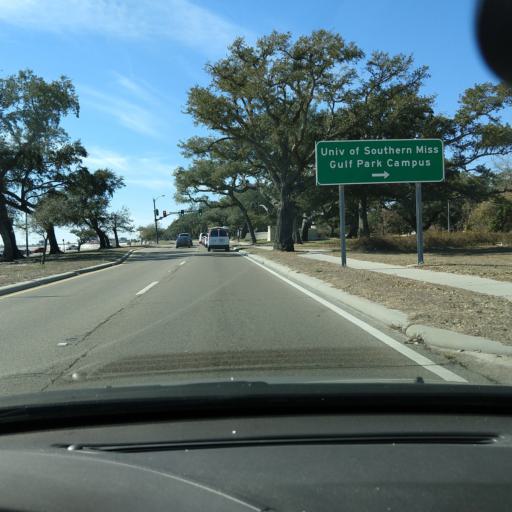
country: US
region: Mississippi
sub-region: Harrison County
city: Long Beach
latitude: 30.3518
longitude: -89.1336
